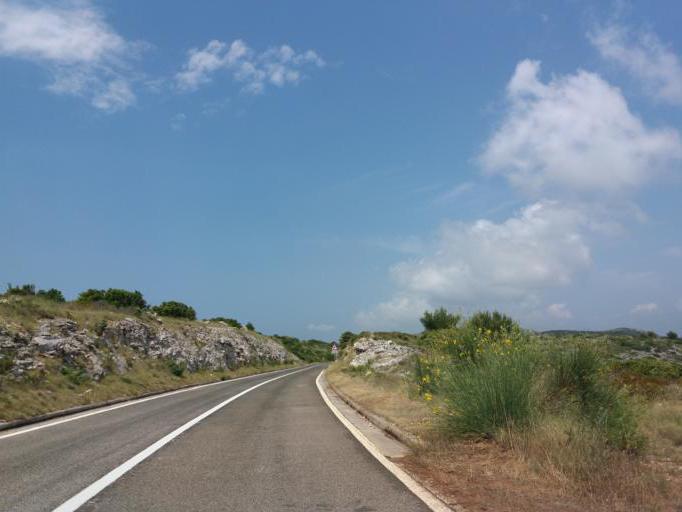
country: HR
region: Zadarska
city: Ugljan
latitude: 44.0271
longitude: 15.0292
